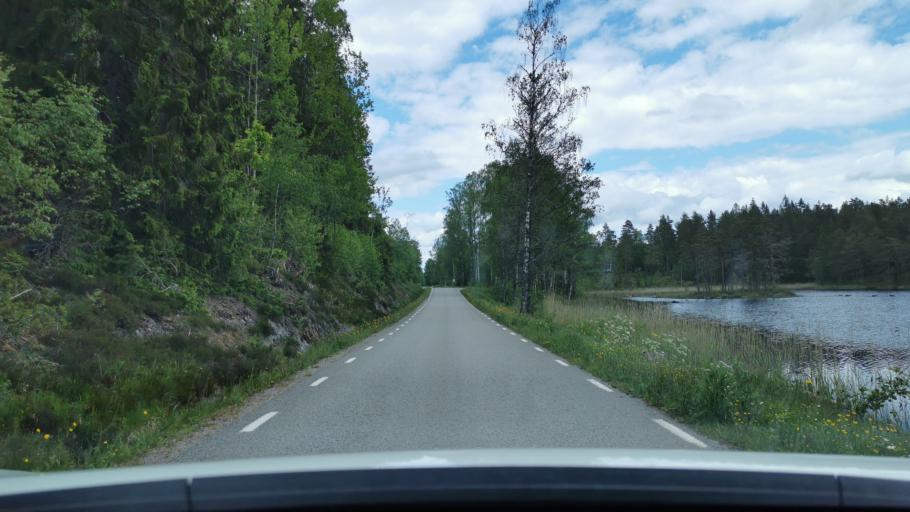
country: SE
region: Vaestra Goetaland
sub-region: Bengtsfors Kommun
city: Dals Langed
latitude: 58.8602
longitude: 12.3275
